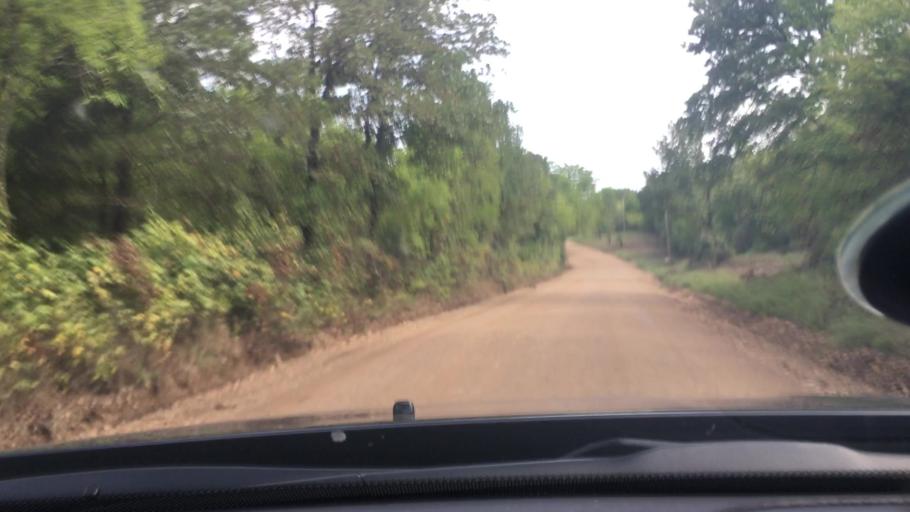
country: US
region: Oklahoma
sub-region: Atoka County
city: Atoka
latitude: 34.4443
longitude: -96.0672
